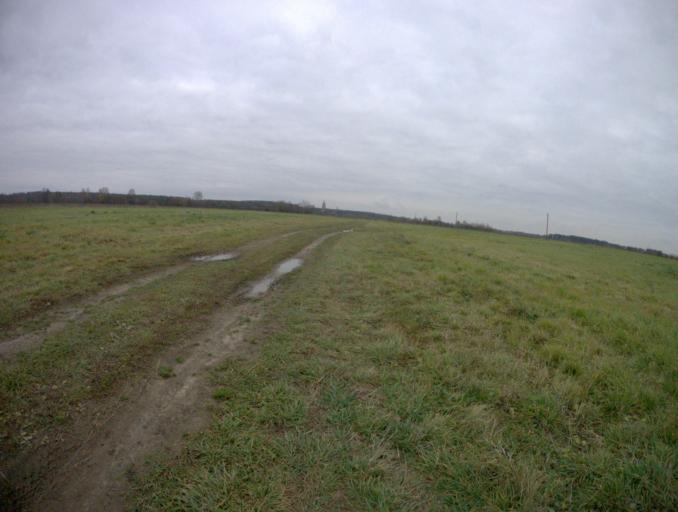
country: RU
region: Moskovskaya
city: Malaya Dubna
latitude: 55.9924
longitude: 38.9802
